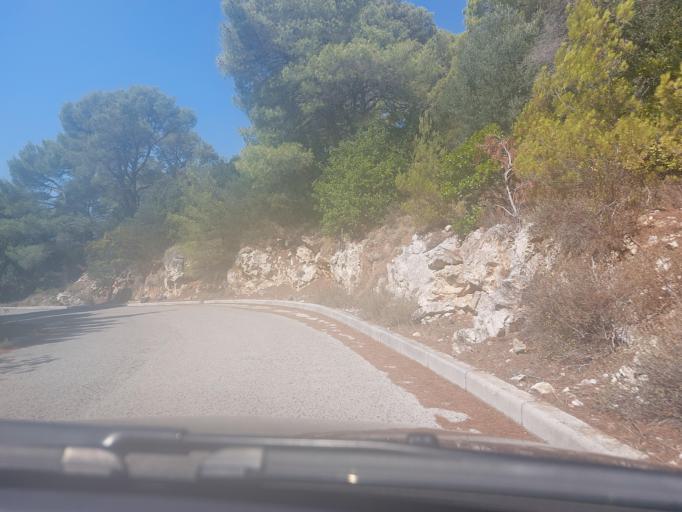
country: HR
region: Dubrovacko-Neretvanska
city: Smokvica
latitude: 42.7492
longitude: 16.8442
